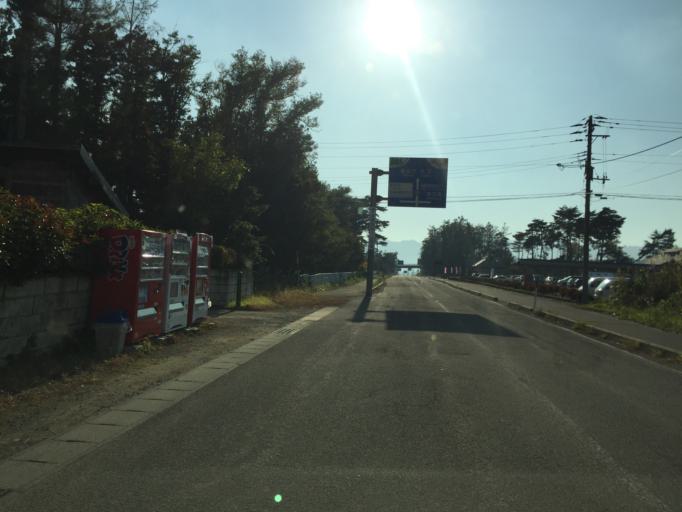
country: JP
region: Fukushima
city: Kitakata
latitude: 37.7218
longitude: 139.8734
